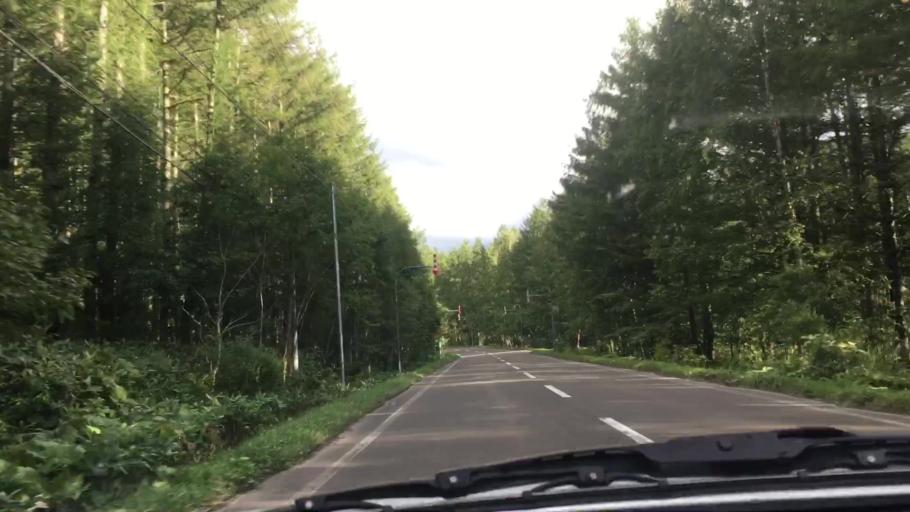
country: JP
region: Hokkaido
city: Shimo-furano
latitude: 43.1171
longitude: 142.6826
